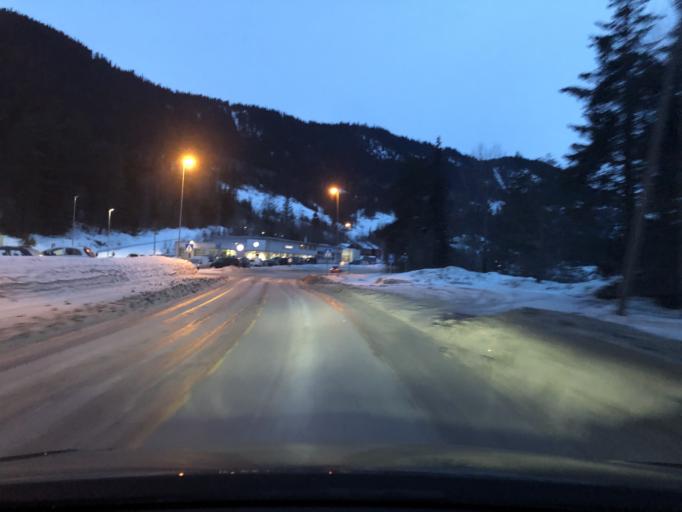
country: NO
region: Oppland
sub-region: Nord-Aurdal
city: Fagernes
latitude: 60.9900
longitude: 9.2237
